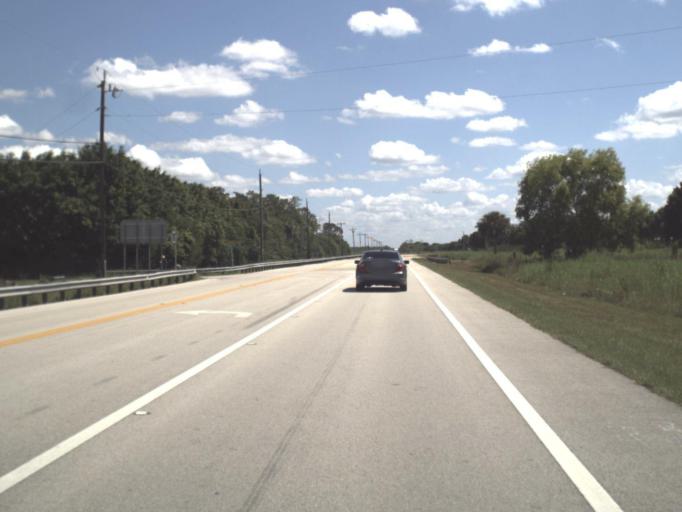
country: US
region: Florida
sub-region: Collier County
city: Lely Resort
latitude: 26.0189
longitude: -81.6298
